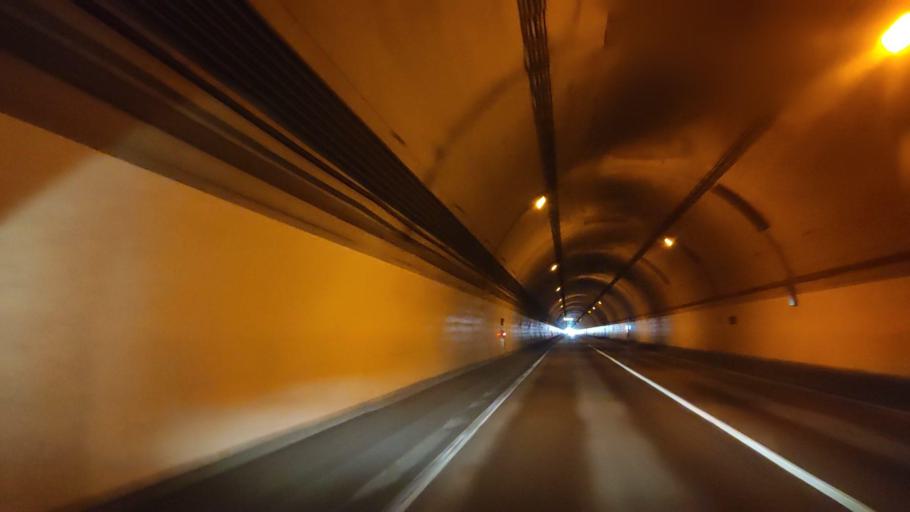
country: JP
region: Hokkaido
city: Rumoi
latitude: 43.8212
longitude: 141.4503
